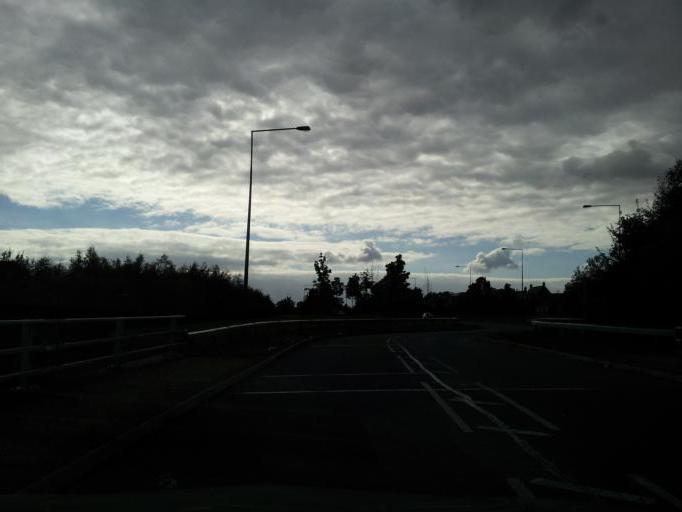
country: GB
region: England
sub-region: Milton Keynes
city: Shenley Church End
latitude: 52.0038
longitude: -0.8054
